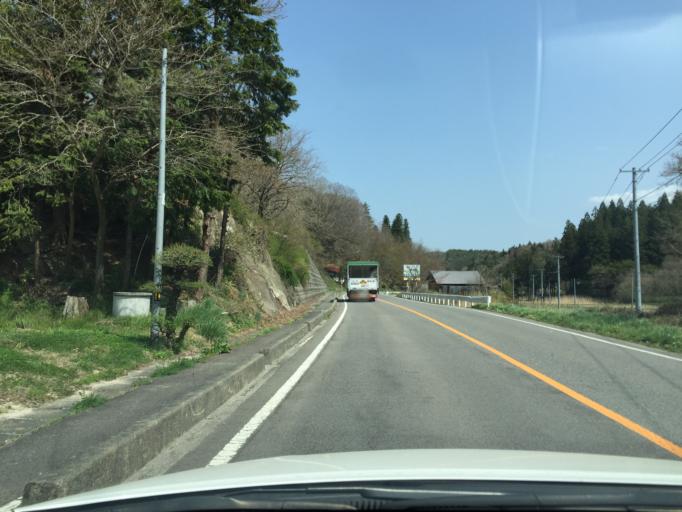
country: JP
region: Fukushima
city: Funehikimachi-funehiki
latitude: 37.4584
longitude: 140.7276
